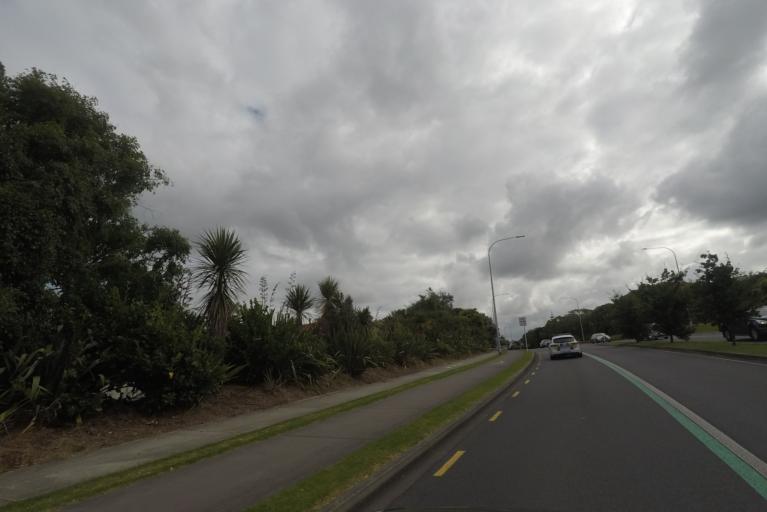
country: NZ
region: Auckland
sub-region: Auckland
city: Rothesay Bay
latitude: -36.7327
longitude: 174.6931
